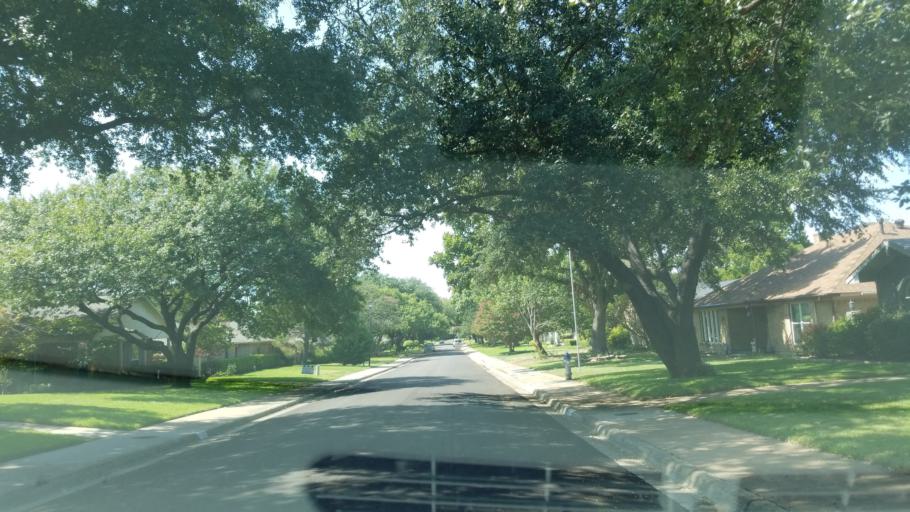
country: US
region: Texas
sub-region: Dallas County
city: Addison
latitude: 32.9687
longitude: -96.7795
